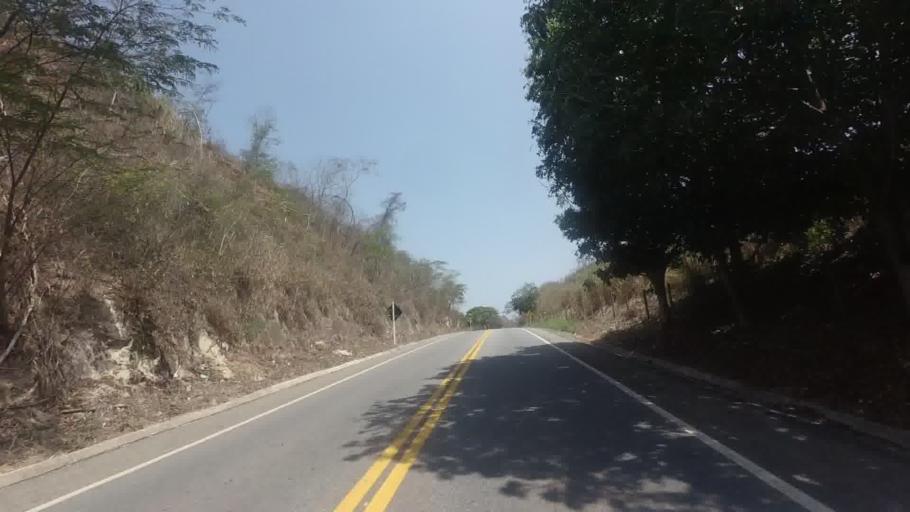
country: BR
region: Espirito Santo
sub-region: Mimoso Do Sul
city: Mimoso do Sul
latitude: -20.9306
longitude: -41.3202
